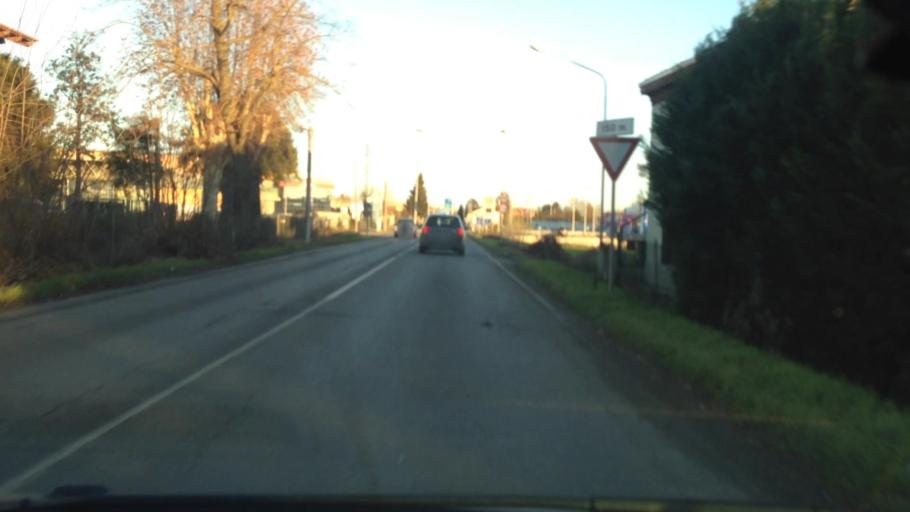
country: IT
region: Piedmont
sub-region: Provincia di Alessandria
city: Alessandria
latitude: 44.9219
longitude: 8.5801
